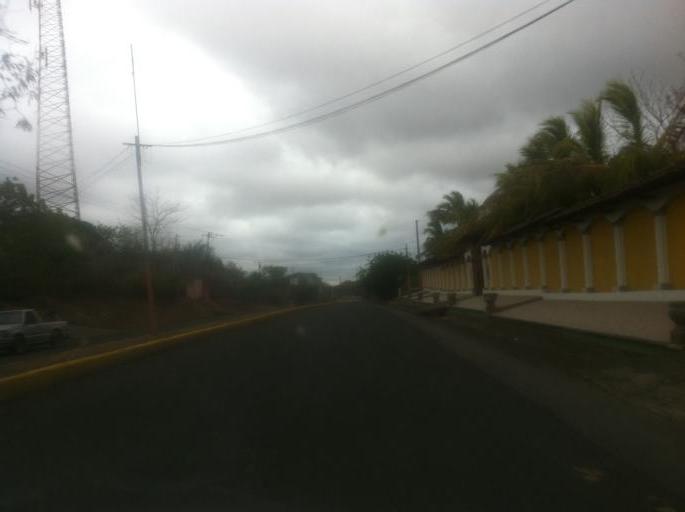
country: NI
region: Granada
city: Granada
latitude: 11.9519
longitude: -85.9864
